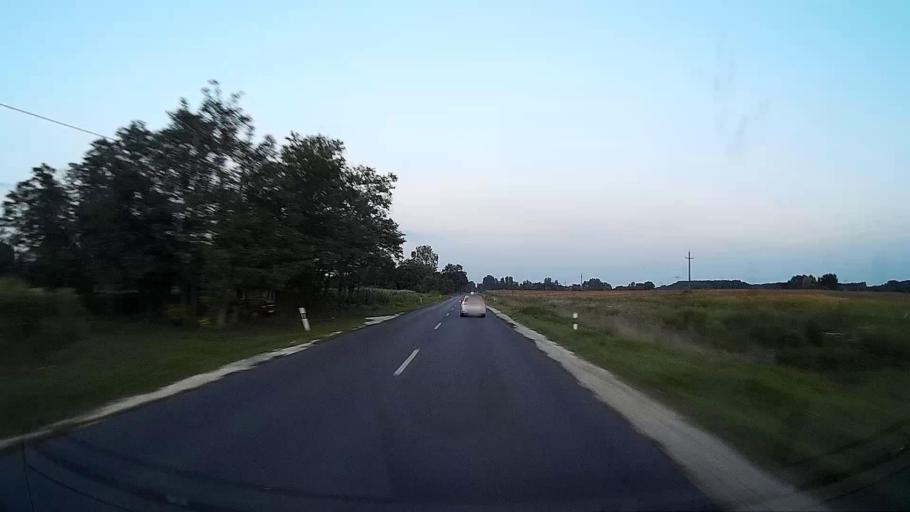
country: HU
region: Pest
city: Albertirsa
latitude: 47.2444
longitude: 19.6325
